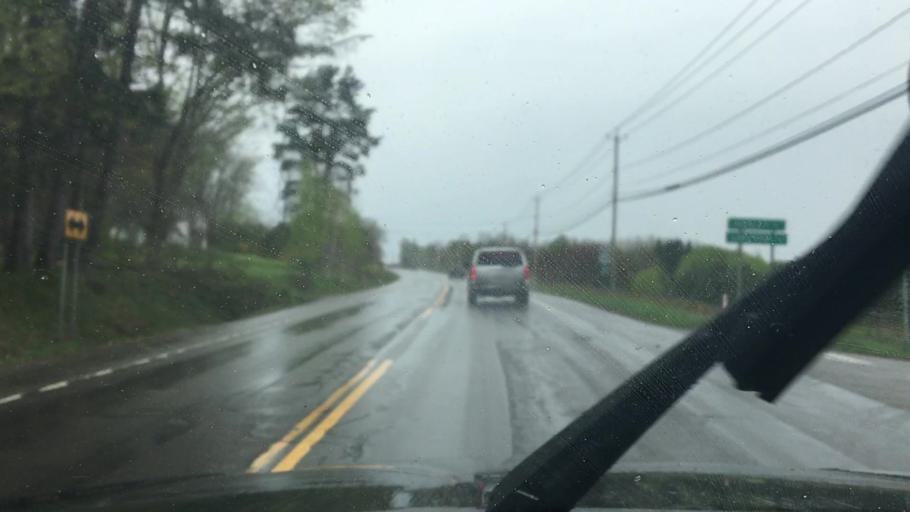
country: US
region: New York
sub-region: Chautauqua County
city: Lakewood
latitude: 42.1345
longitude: -79.3967
